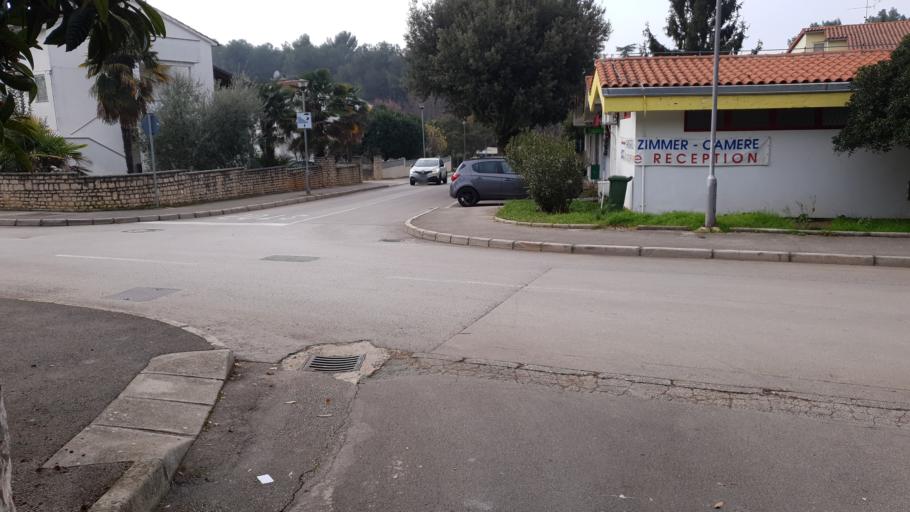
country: HR
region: Istarska
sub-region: Grad Porec
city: Porec
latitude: 45.2205
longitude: 13.5972
